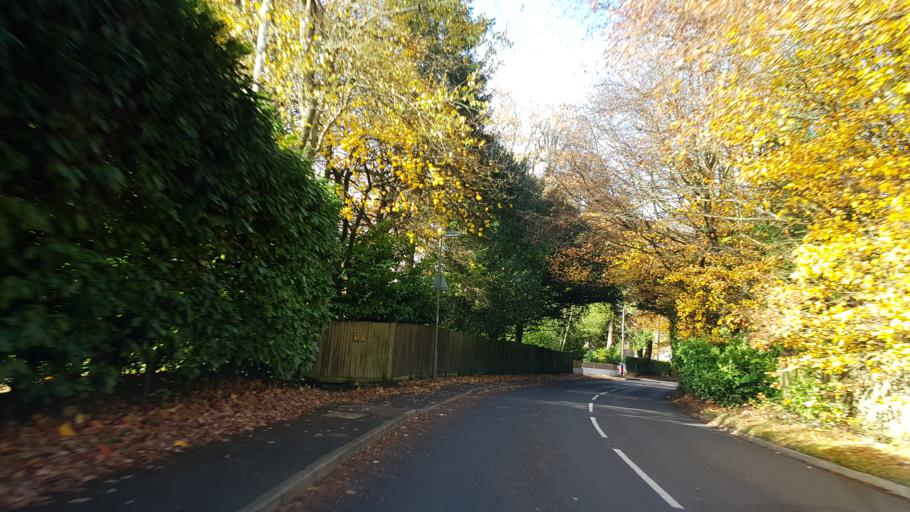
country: GB
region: England
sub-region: Surrey
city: Hindhead
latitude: 51.1205
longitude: -0.7405
